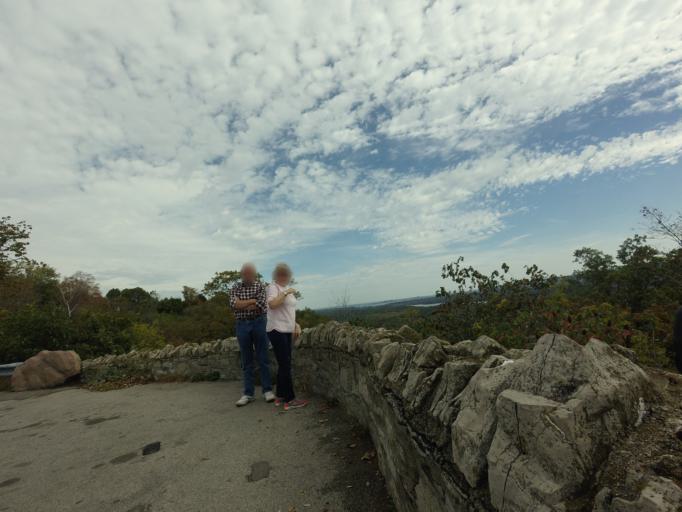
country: CA
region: Ontario
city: Ancaster
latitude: 43.2776
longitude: -79.9497
